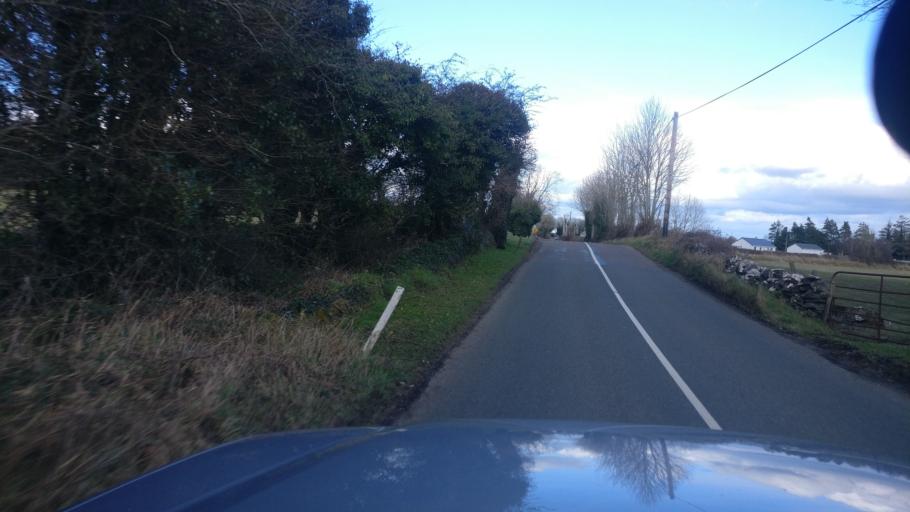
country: IE
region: Connaught
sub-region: County Galway
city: Loughrea
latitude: 53.2135
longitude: -8.4019
